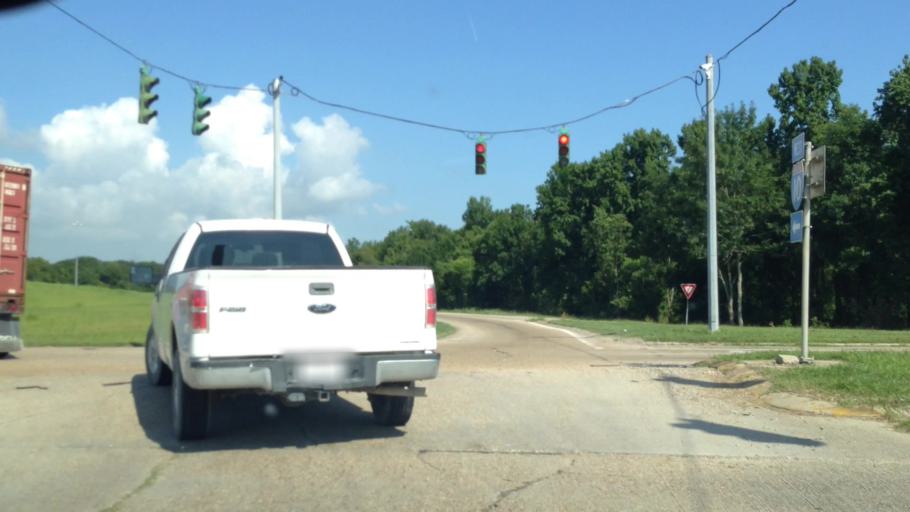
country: US
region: Louisiana
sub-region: Ascension Parish
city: Sorrento
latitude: 30.1725
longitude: -90.8760
